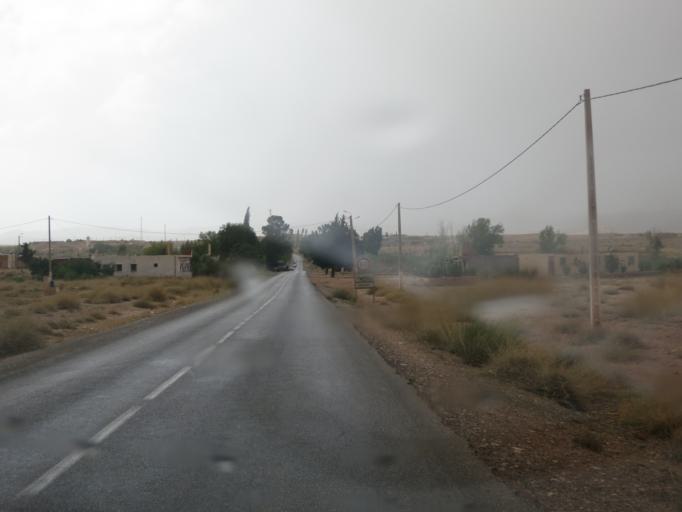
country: MA
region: Meknes-Tafilalet
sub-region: Khenifra
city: Itzer
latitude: 32.8782
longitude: -4.9476
